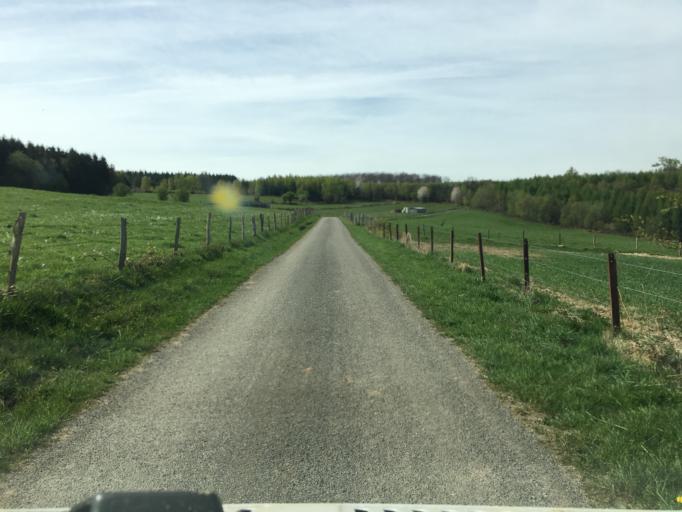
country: BE
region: Wallonia
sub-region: Province de Liege
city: Aywaille
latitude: 50.4330
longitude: 5.6581
